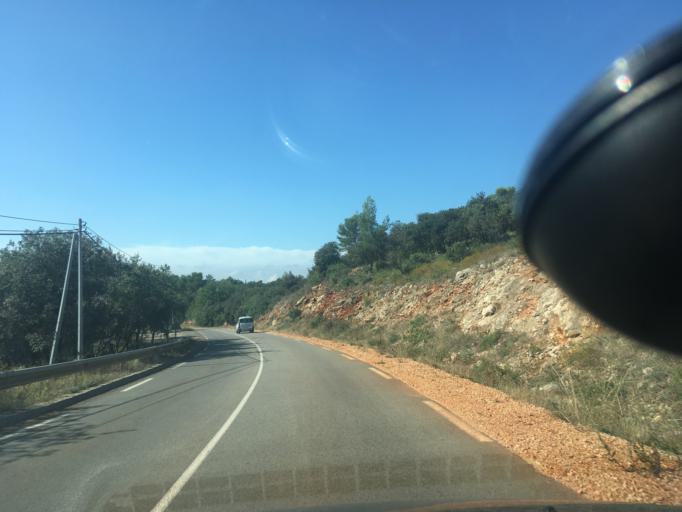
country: FR
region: Provence-Alpes-Cote d'Azur
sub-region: Departement du Var
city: Barjols
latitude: 43.5985
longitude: 6.0395
